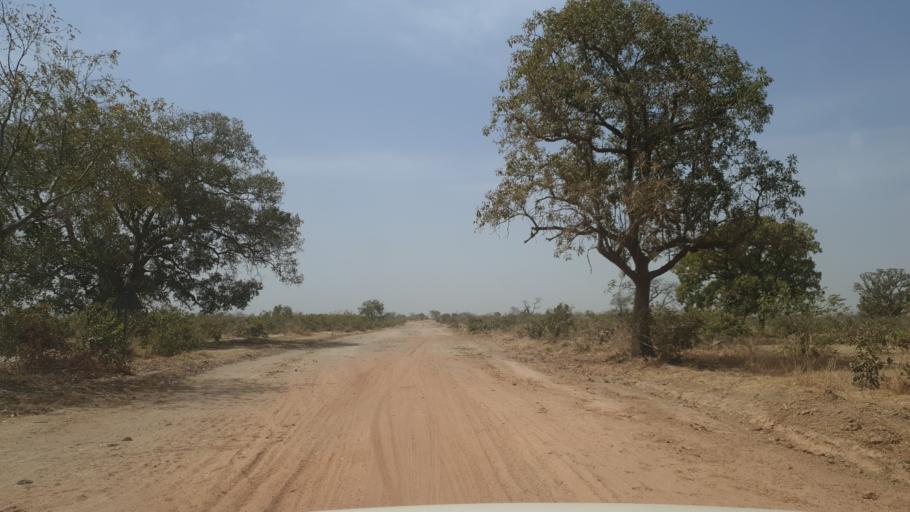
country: ML
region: Koulikoro
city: Kolokani
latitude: 13.4732
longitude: -8.1893
